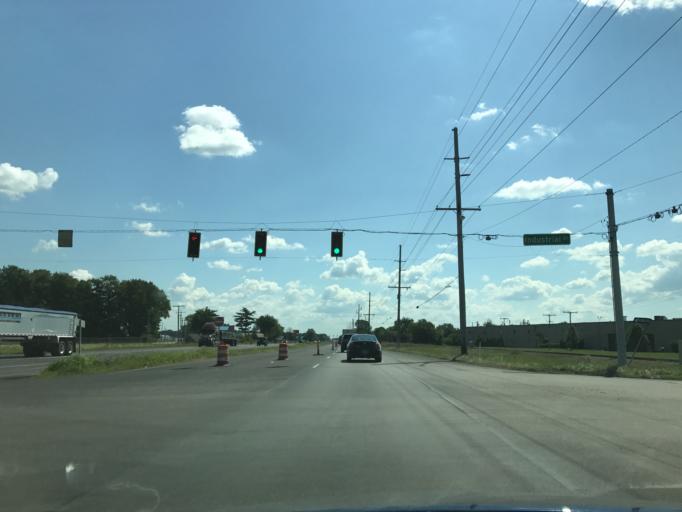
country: US
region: Indiana
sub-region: Porter County
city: Valparaiso
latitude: 41.4490
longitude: -87.0172
